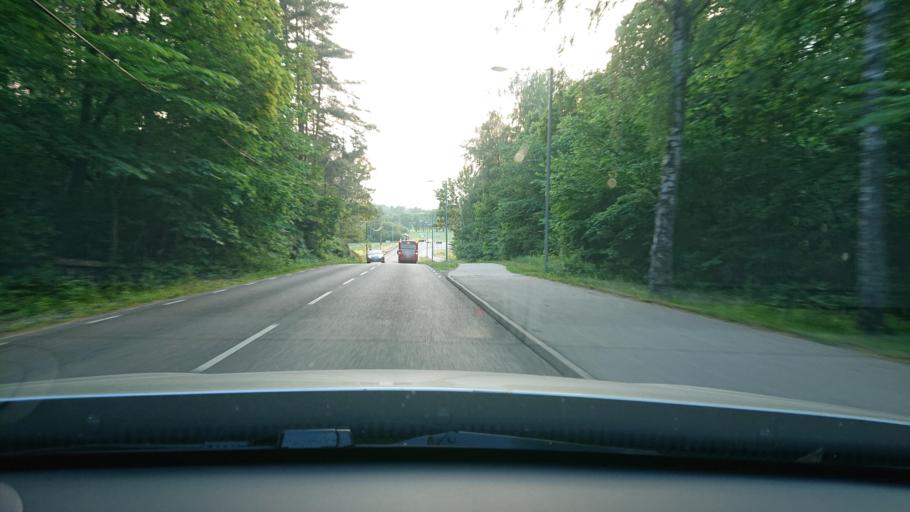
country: SE
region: Stockholm
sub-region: Vaxholms Kommun
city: Resaro
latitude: 59.4620
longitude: 18.3449
